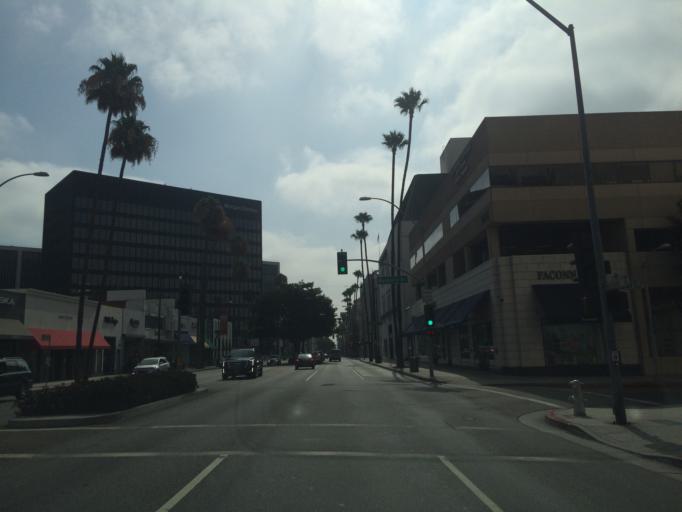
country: US
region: California
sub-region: Los Angeles County
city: Beverly Hills
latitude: 34.0670
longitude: -118.4060
